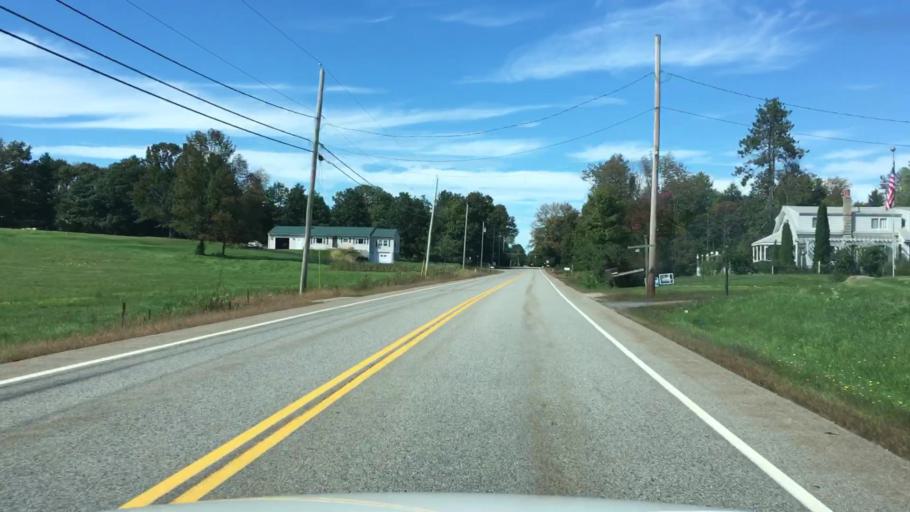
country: US
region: Maine
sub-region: Cumberland County
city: Westbrook
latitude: 43.6684
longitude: -70.4080
